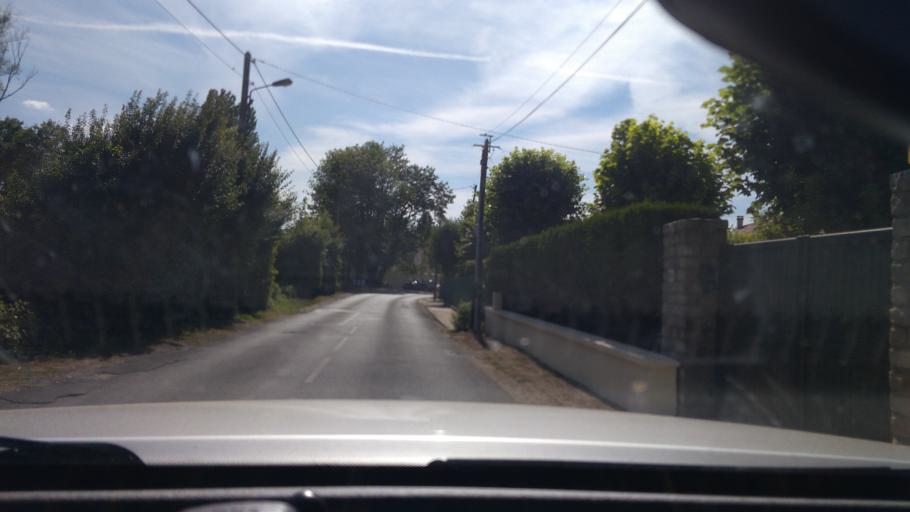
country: FR
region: Ile-de-France
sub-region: Departement de Seine-et-Marne
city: Chartrettes
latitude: 48.4854
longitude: 2.7120
